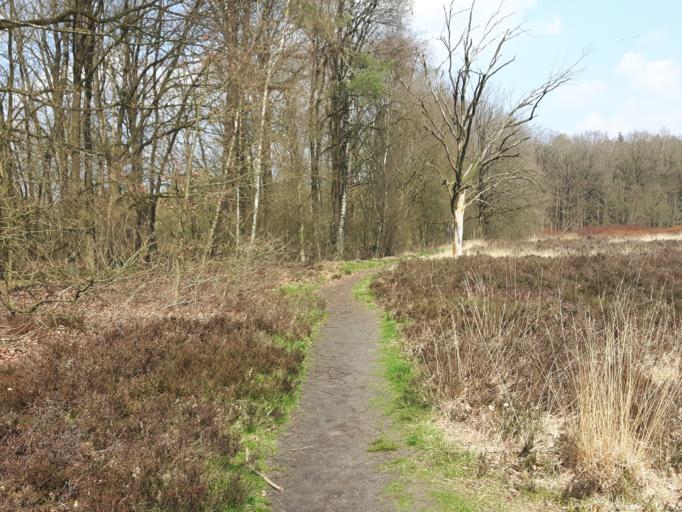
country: NL
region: Overijssel
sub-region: Gemeente Haaksbergen
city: Haaksbergen
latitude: 52.1668
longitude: 6.8088
